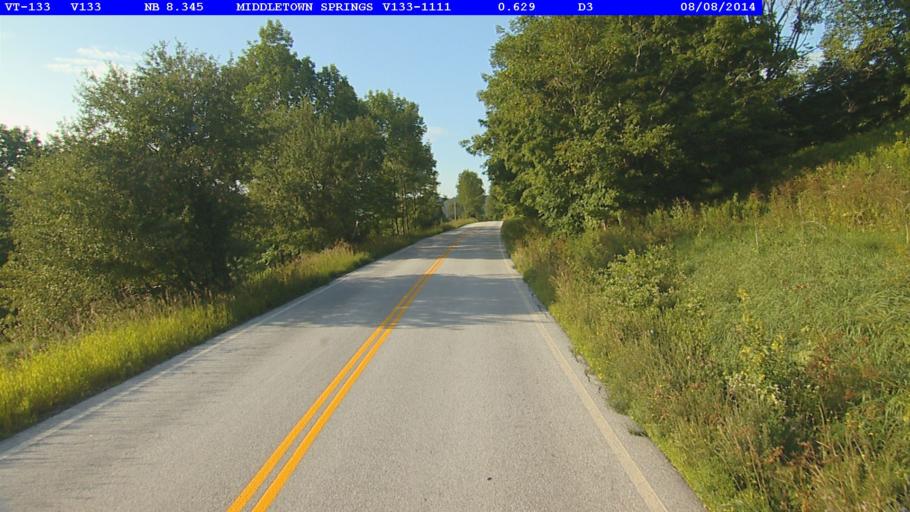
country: US
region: Vermont
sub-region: Rutland County
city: Poultney
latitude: 43.4446
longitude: -73.1111
